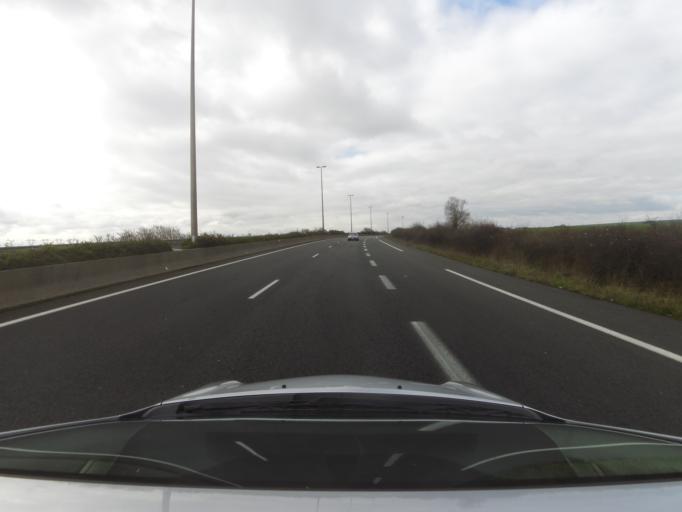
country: FR
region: Nord-Pas-de-Calais
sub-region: Departement du Pas-de-Calais
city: Coquelles
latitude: 50.9105
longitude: 1.7833
